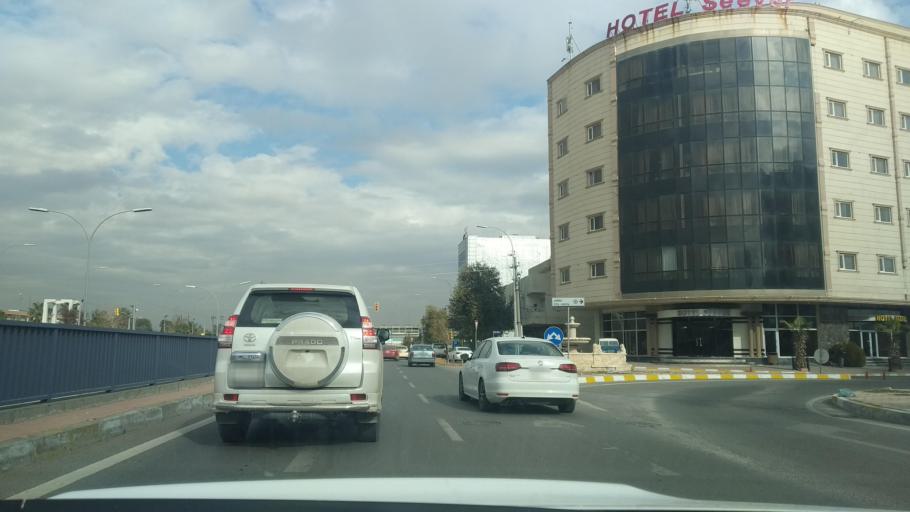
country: IQ
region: Arbil
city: Erbil
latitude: 36.1890
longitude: 43.9939
